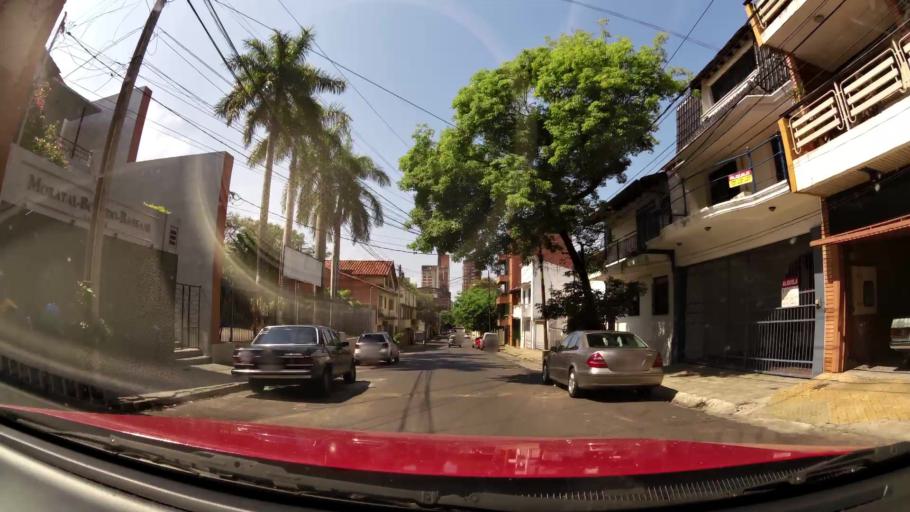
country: PY
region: Asuncion
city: Asuncion
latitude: -25.2854
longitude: -57.6424
